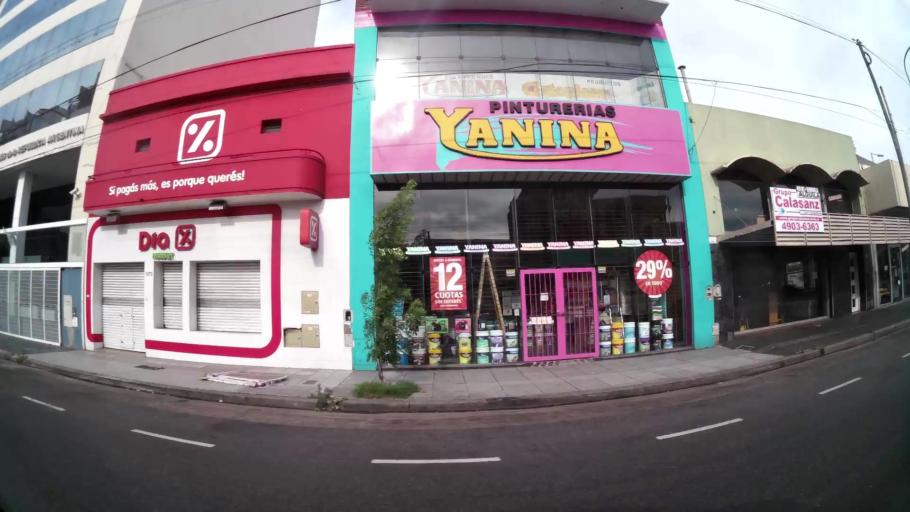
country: AR
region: Buenos Aires F.D.
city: Buenos Aires
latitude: -34.6334
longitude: -58.4252
